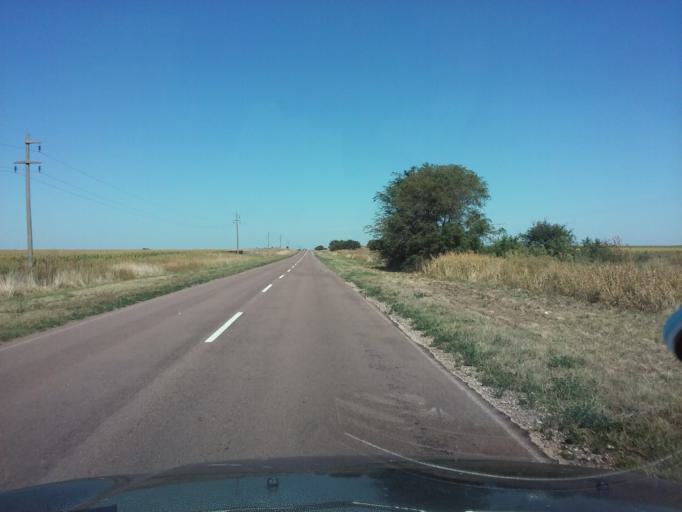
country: AR
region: La Pampa
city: Anguil
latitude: -36.4784
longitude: -63.9436
